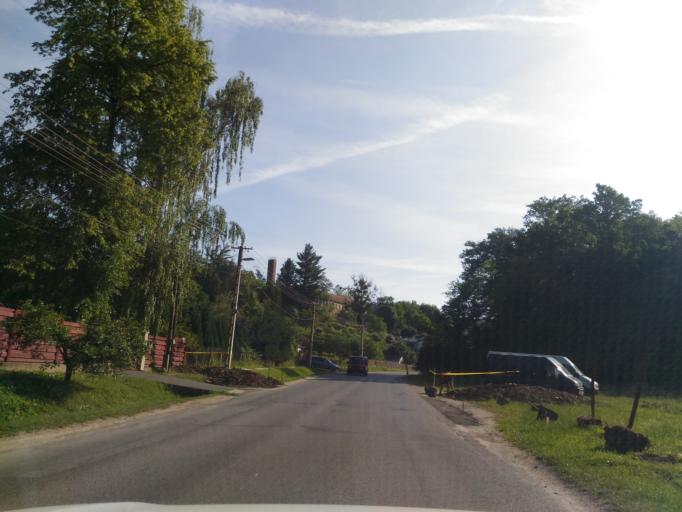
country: HU
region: Baranya
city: Komlo
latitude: 46.1846
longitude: 18.2927
